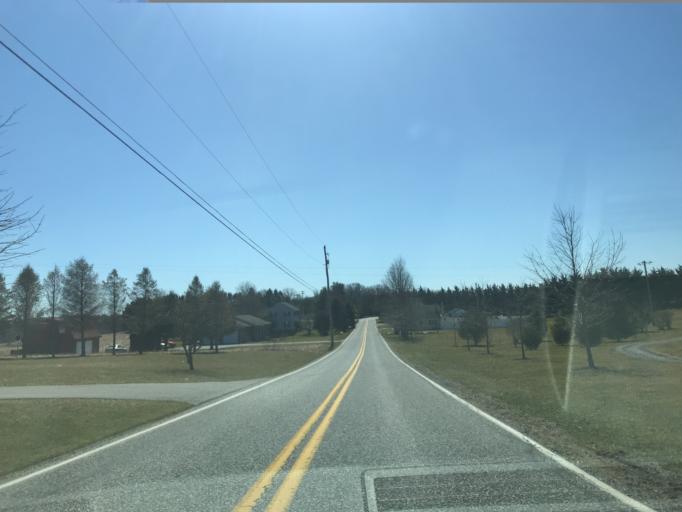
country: US
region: Pennsylvania
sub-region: York County
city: Shrewsbury
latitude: 39.7511
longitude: -76.6589
